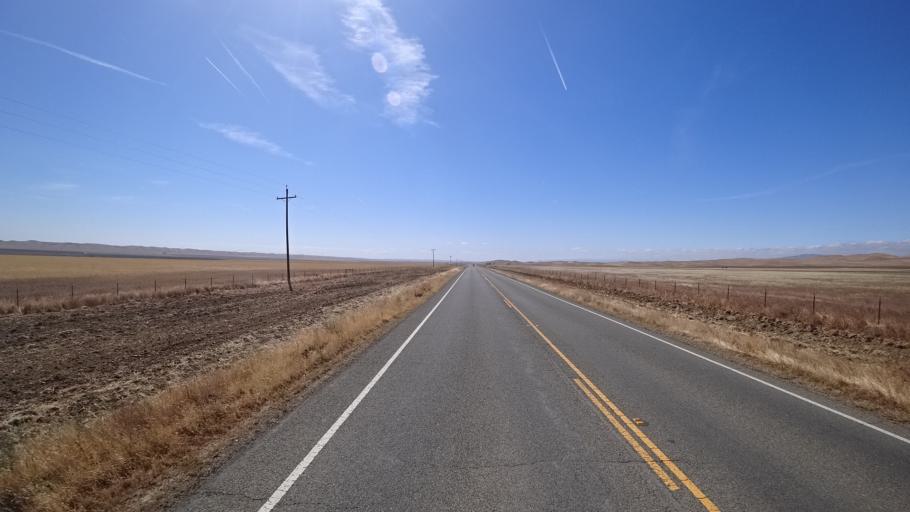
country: US
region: California
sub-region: Kings County
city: Avenal
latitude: 35.9281
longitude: -120.0792
